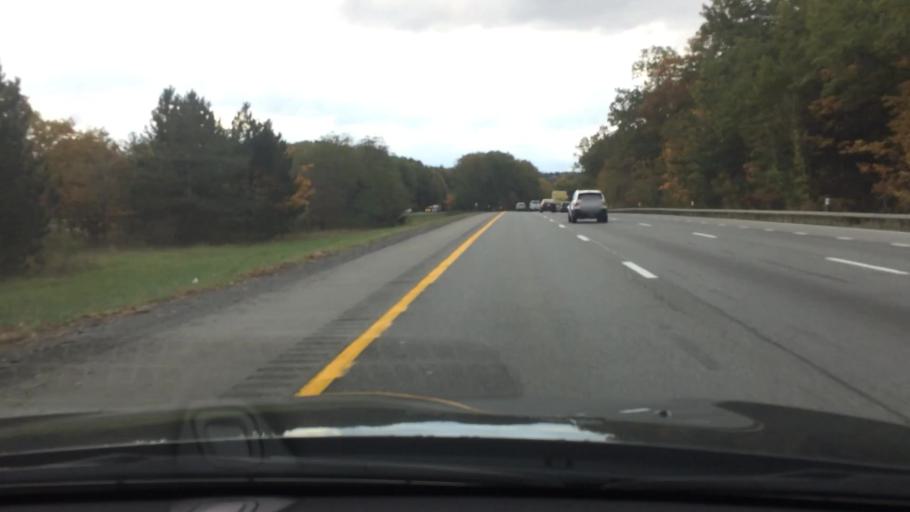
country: US
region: New York
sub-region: Saratoga County
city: Country Knolls
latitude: 42.8994
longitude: -73.7840
